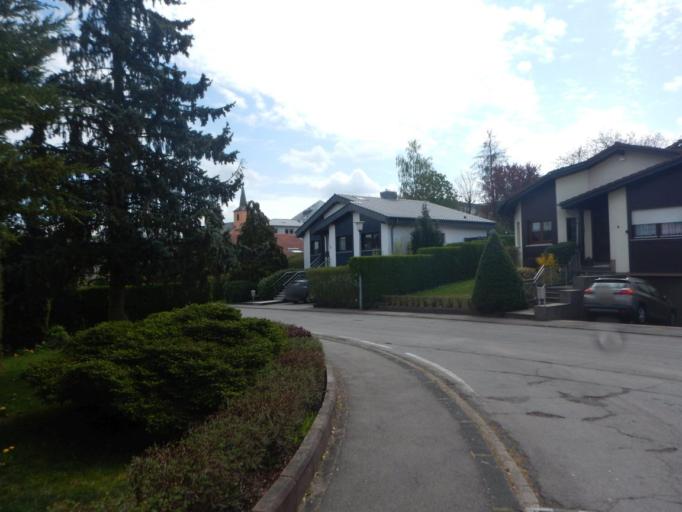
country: LU
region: Grevenmacher
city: Gonderange
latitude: 49.6948
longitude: 6.2480
